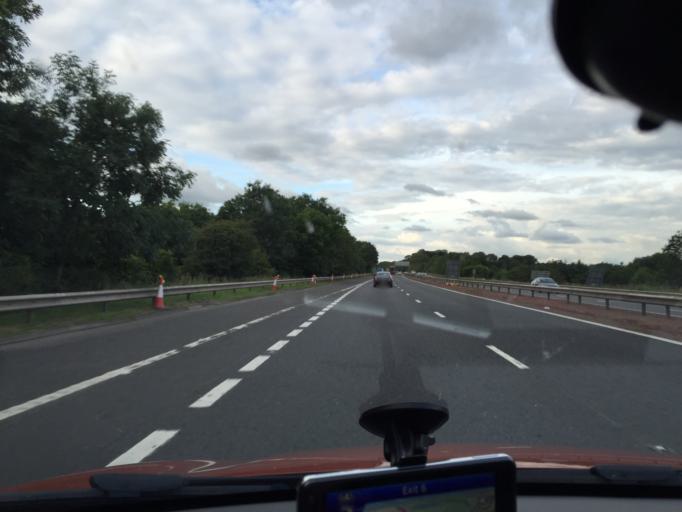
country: GB
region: Scotland
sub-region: South Lanarkshire
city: Uddingston
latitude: 55.8590
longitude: -4.0861
